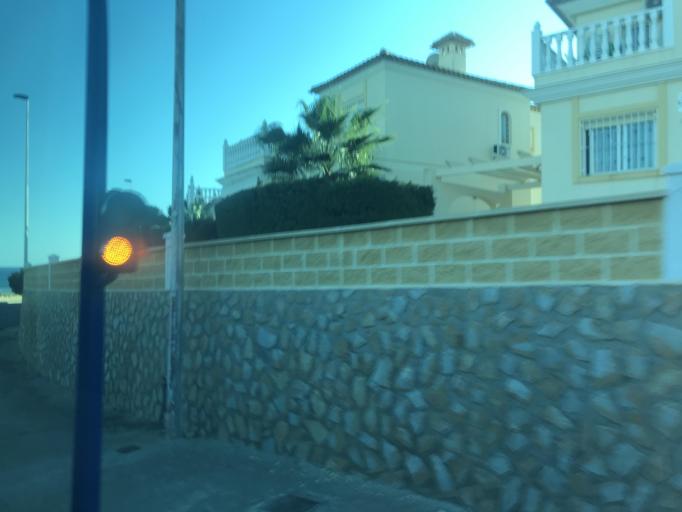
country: ES
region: Valencia
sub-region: Provincia de Alicante
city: Torrevieja
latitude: 38.0013
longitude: -0.6520
